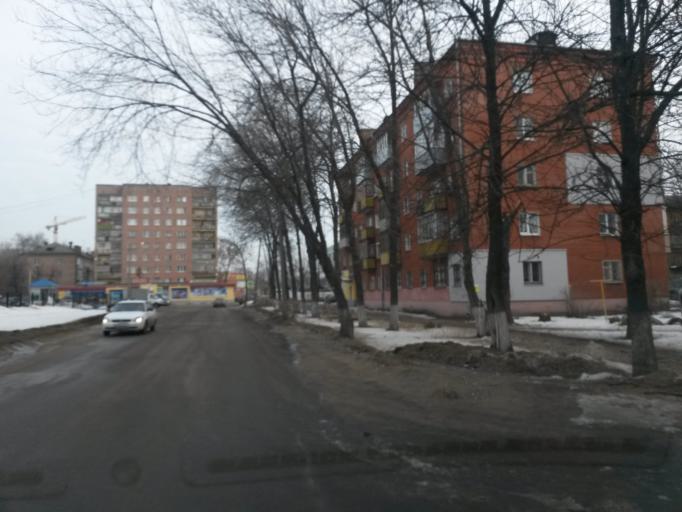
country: RU
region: Jaroslavl
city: Yaroslavl
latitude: 57.6366
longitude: 39.8448
